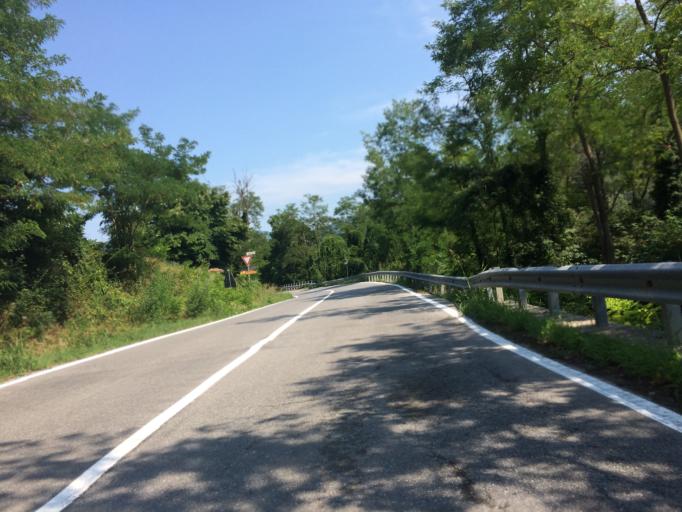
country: IT
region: Piedmont
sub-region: Provincia di Cuneo
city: Cortemilia
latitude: 44.5830
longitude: 8.1741
